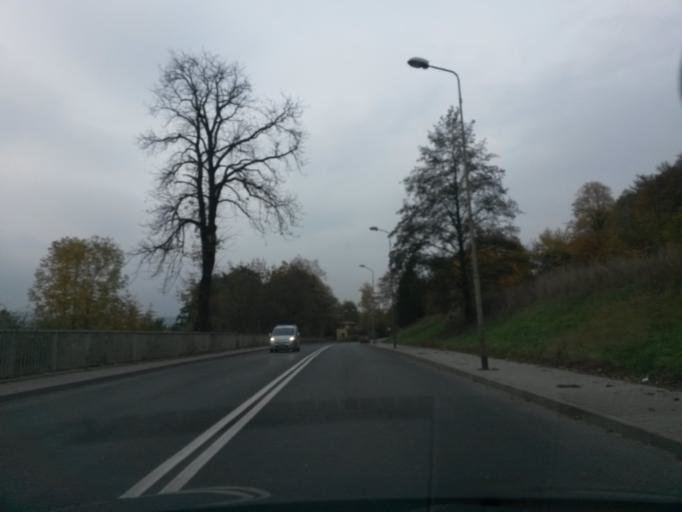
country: PL
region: Lower Silesian Voivodeship
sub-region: Powiat klodzki
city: Klodzko
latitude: 50.4458
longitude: 16.6596
